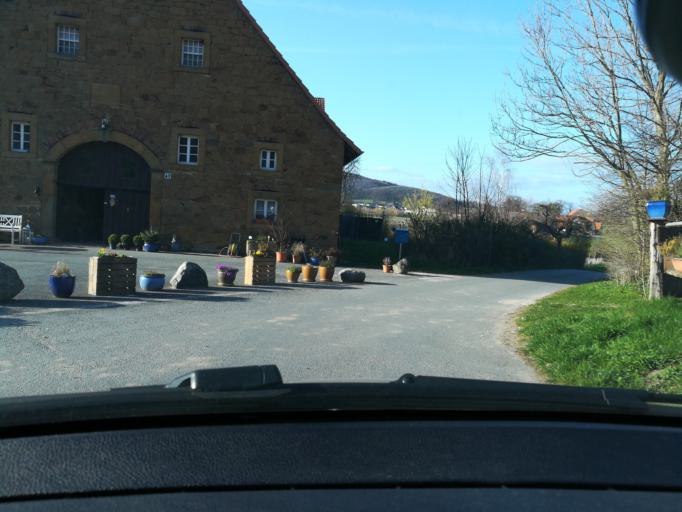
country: DE
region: North Rhine-Westphalia
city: Borgholzhausen
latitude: 52.0864
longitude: 8.2911
